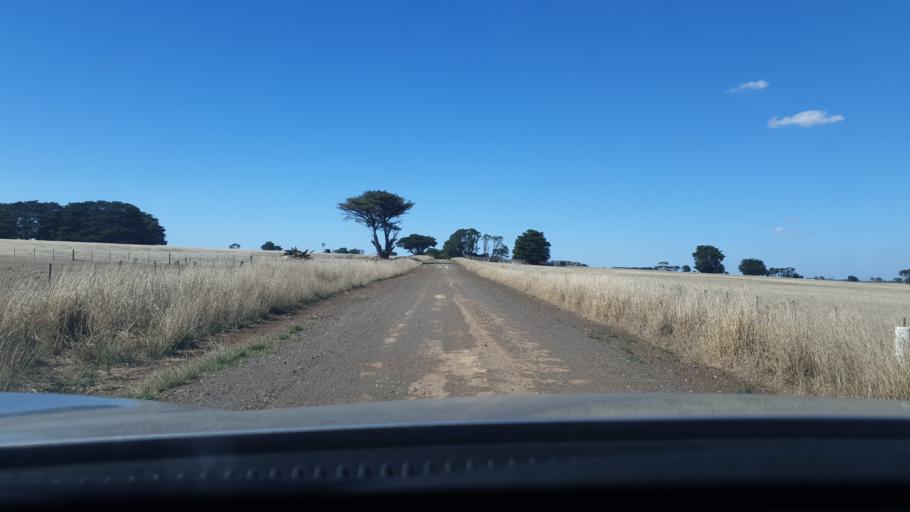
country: AU
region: Victoria
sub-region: Warrnambool
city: Warrnambool
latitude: -38.1649
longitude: 142.3821
